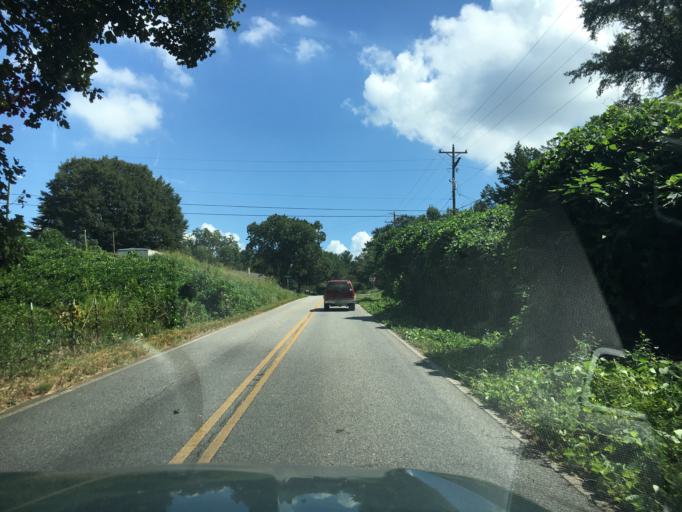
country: US
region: South Carolina
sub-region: Spartanburg County
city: Wellford
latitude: 34.8999
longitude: -82.0558
